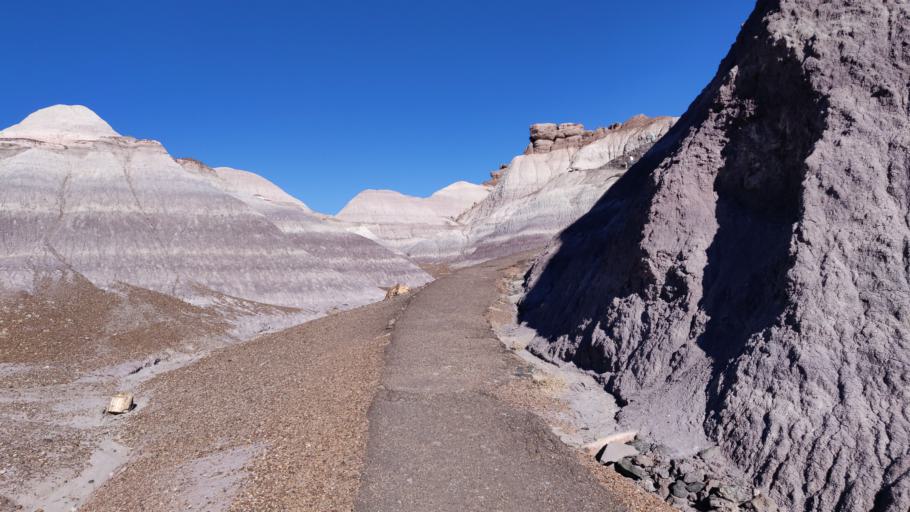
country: US
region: Arizona
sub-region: Navajo County
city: Holbrook
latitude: 34.9390
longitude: -109.7596
